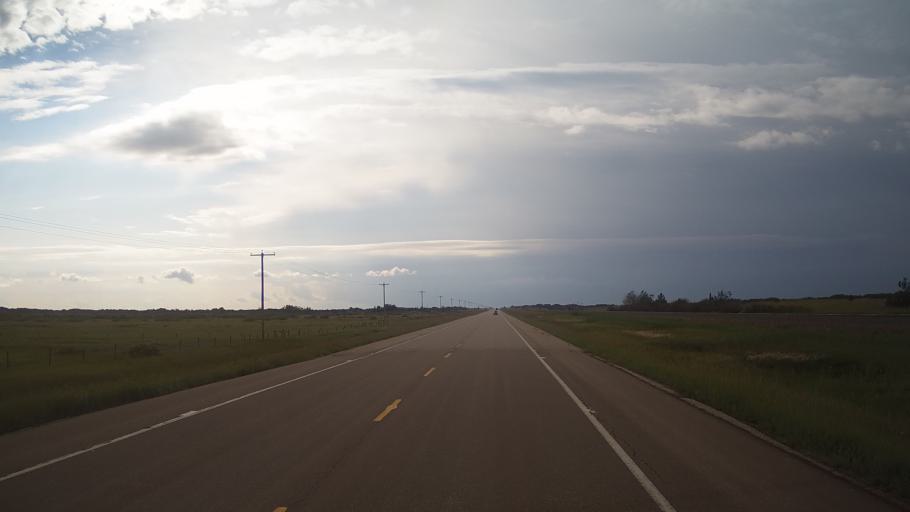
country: CA
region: Alberta
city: Viking
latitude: 53.1416
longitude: -111.9411
